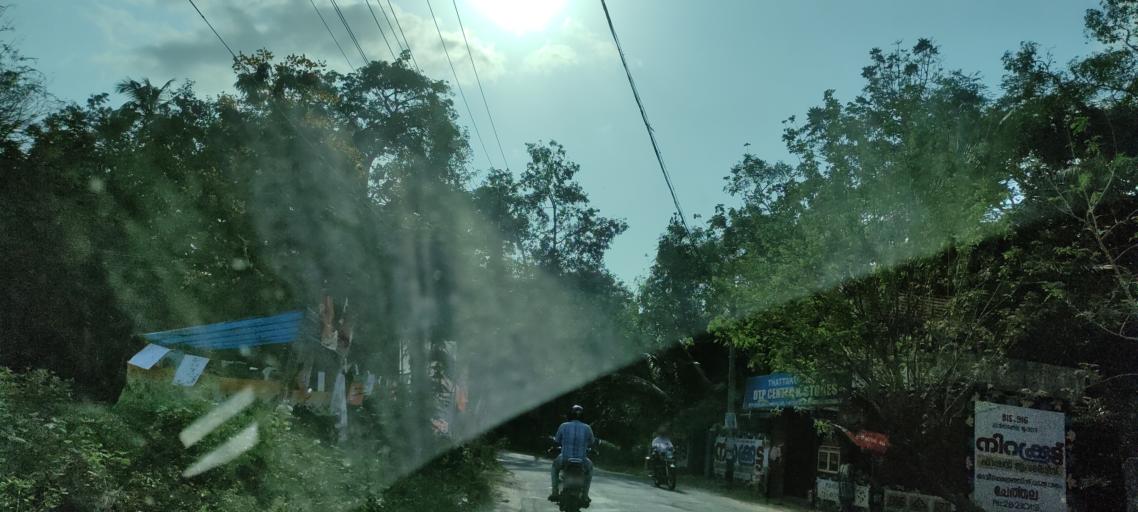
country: IN
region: Kerala
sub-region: Alappuzha
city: Vayalar
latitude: 9.6874
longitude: 76.3122
